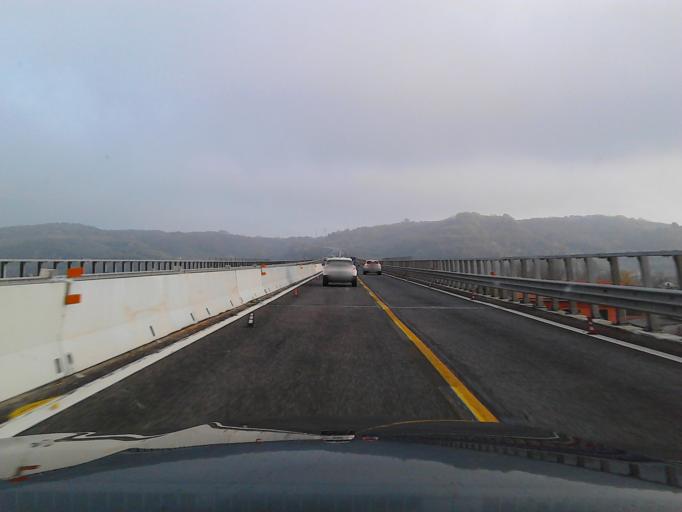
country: IT
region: Abruzzo
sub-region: Provincia di Chieti
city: Miglianico
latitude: 42.3767
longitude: 14.2993
